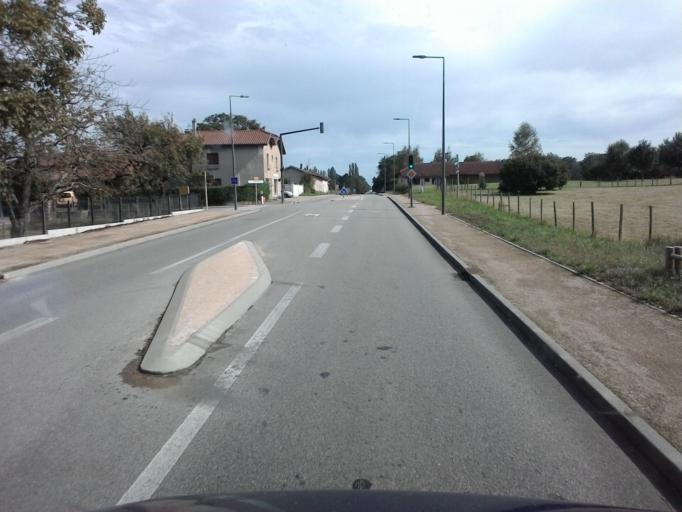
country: FR
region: Rhone-Alpes
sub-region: Departement de l'Ain
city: Mezeriat
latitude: 46.2557
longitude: 5.0607
